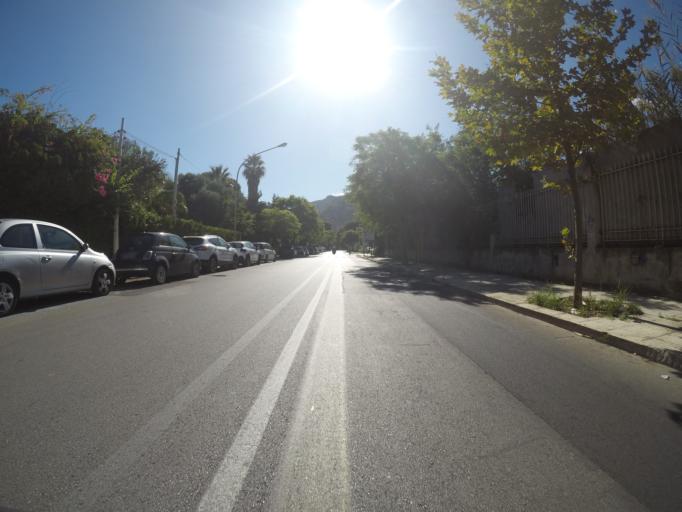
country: IT
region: Sicily
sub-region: Palermo
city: Palermo
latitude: 38.1986
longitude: 13.3282
